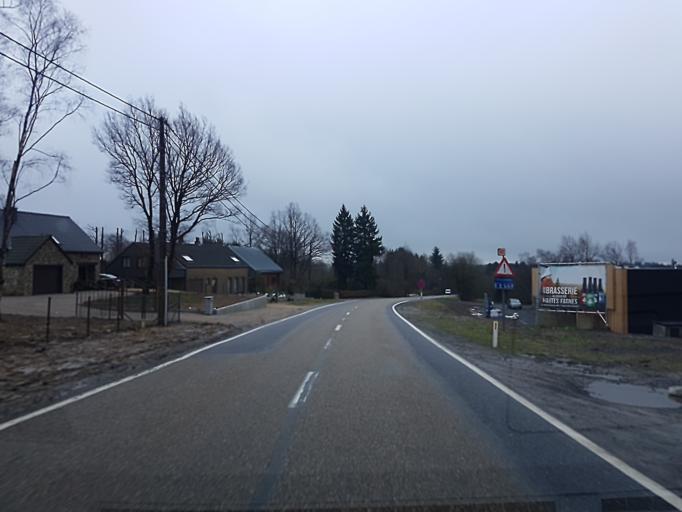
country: BE
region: Wallonia
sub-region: Province de Liege
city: Waimes
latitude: 50.4872
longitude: 6.1094
